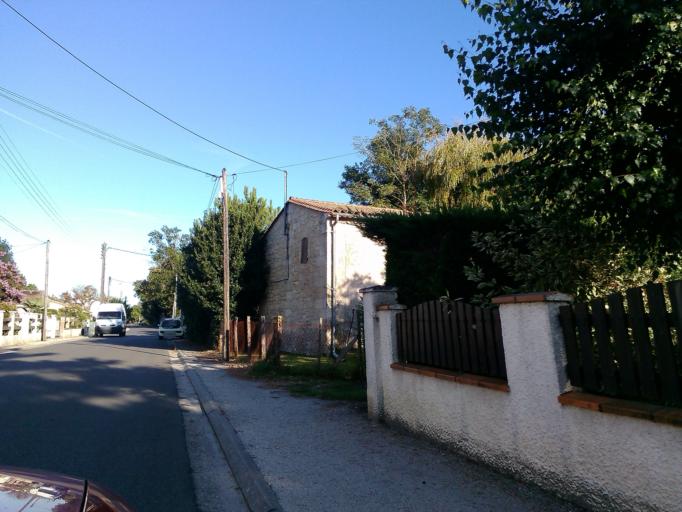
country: FR
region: Aquitaine
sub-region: Departement de la Gironde
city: Soulac-sur-Mer
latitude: 45.4302
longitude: -1.0329
